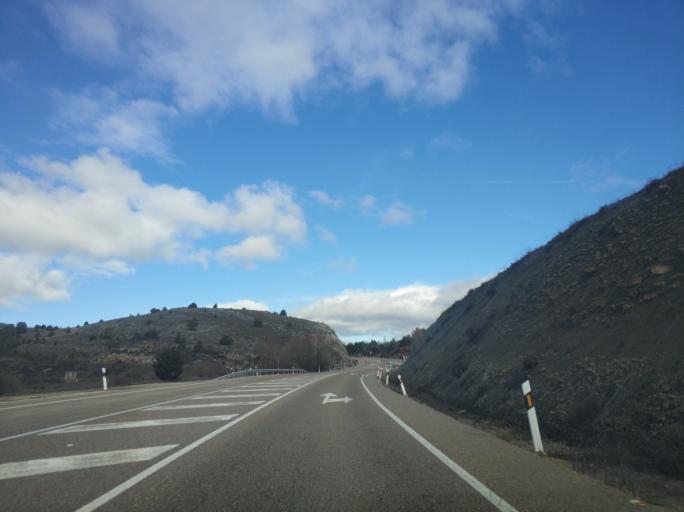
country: ES
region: Castille and Leon
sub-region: Provincia de Burgos
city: Rabanera del Pinar
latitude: 41.8817
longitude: -3.2277
